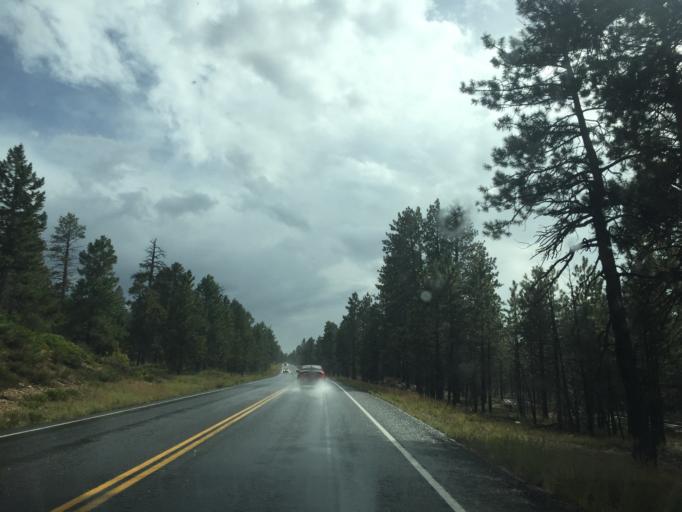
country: US
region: Utah
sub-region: Garfield County
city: Panguitch
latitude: 37.6502
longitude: -112.1644
